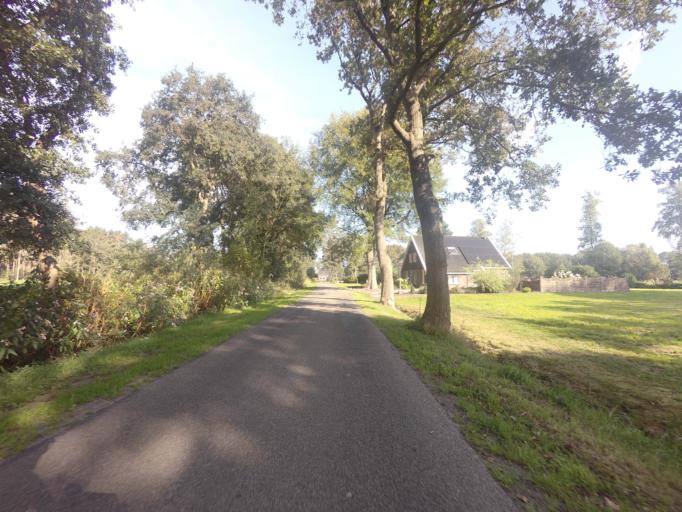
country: NL
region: Groningen
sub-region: Gemeente Leek
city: Leek
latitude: 53.1557
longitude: 6.4338
